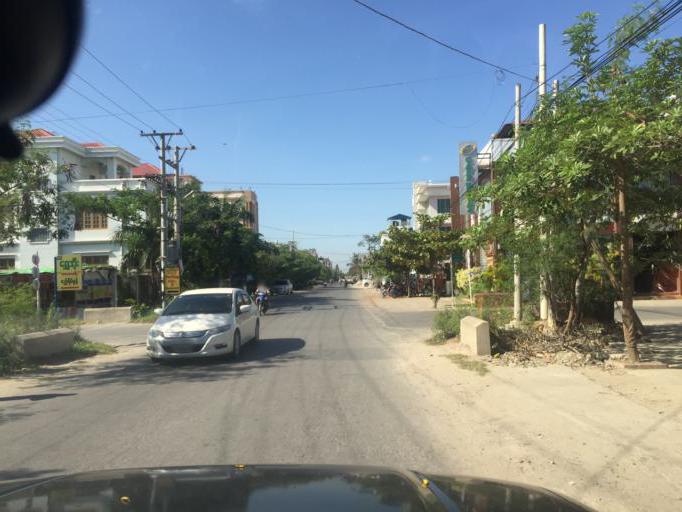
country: MM
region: Mandalay
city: Mandalay
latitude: 21.9591
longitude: 96.1100
